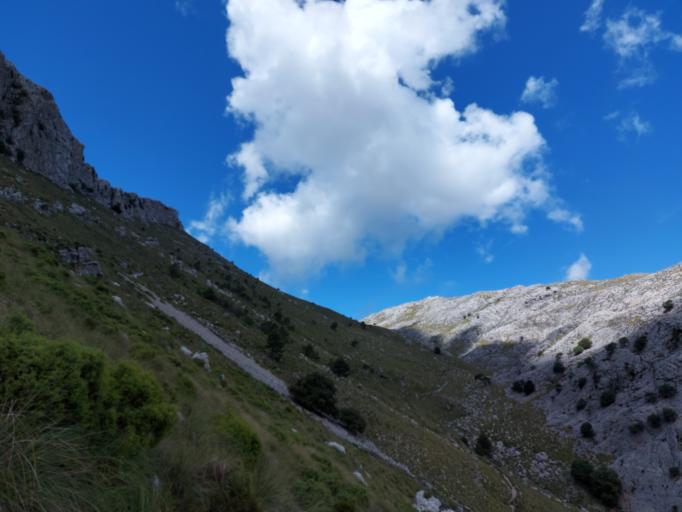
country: ES
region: Balearic Islands
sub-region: Illes Balears
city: Escorca
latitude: 39.8059
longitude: 2.8679
